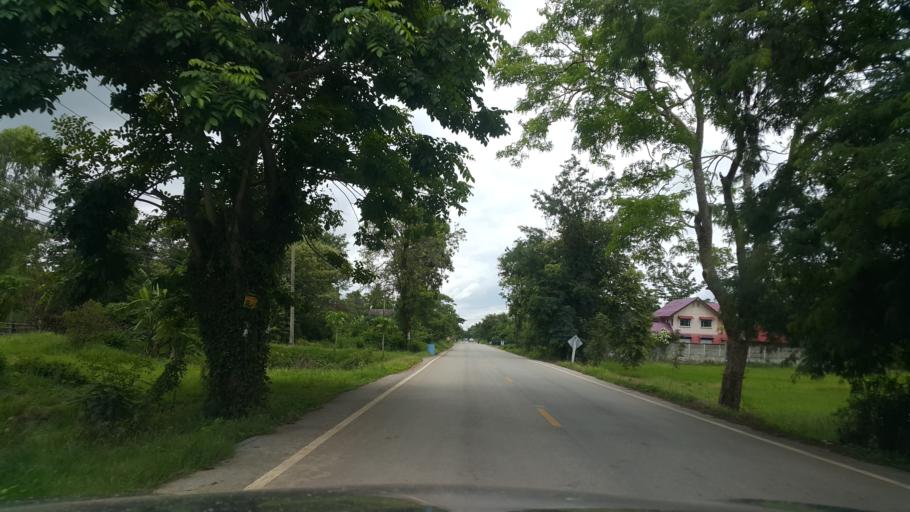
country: TH
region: Sukhothai
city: Kong Krailat
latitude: 16.9091
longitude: 99.8789
